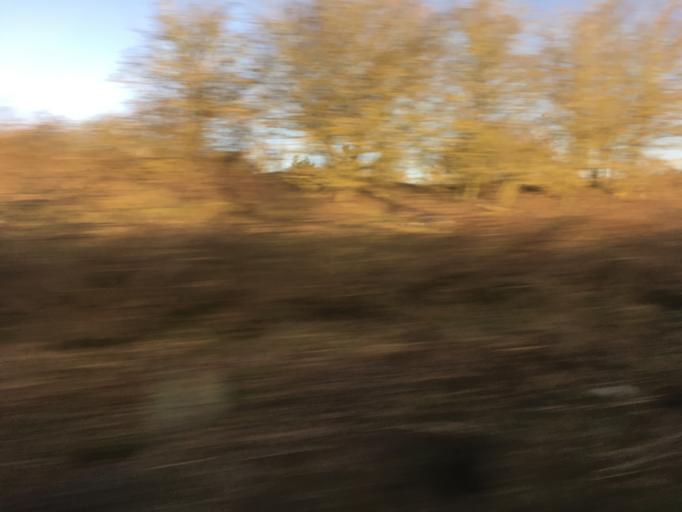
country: GB
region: England
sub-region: Borough of Swindon
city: Wanborough
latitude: 51.5791
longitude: -1.7308
